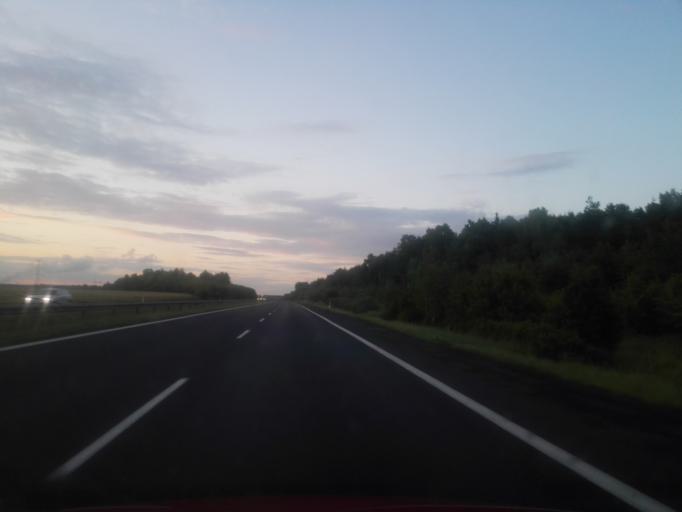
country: PL
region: Lodz Voivodeship
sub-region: Powiat radomszczanski
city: Radomsko
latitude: 51.0678
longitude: 19.3664
